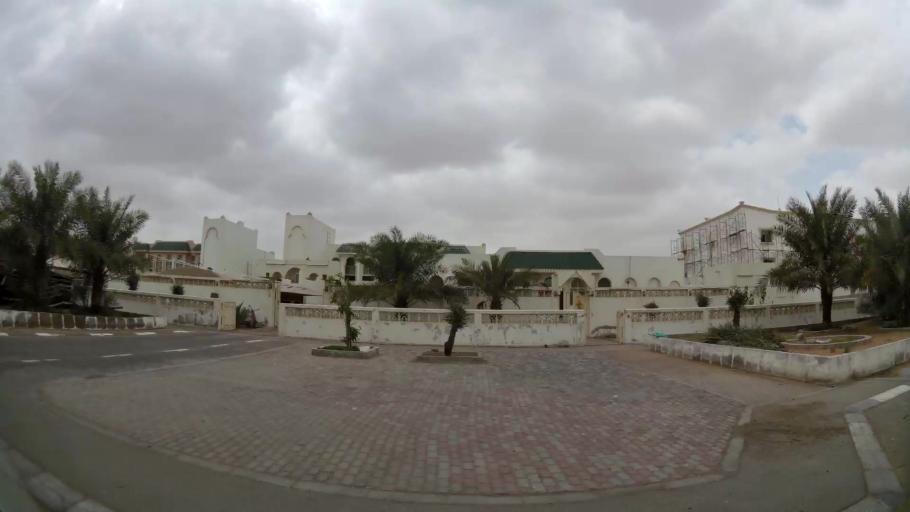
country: AE
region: Abu Dhabi
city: Abu Dhabi
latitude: 24.3319
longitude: 54.6375
